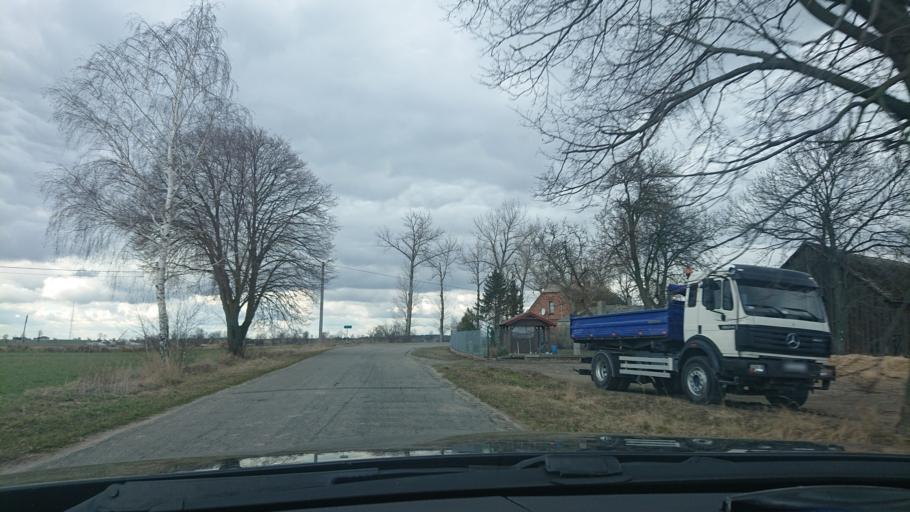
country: PL
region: Greater Poland Voivodeship
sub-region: Powiat gnieznienski
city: Niechanowo
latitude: 52.5844
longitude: 17.7025
